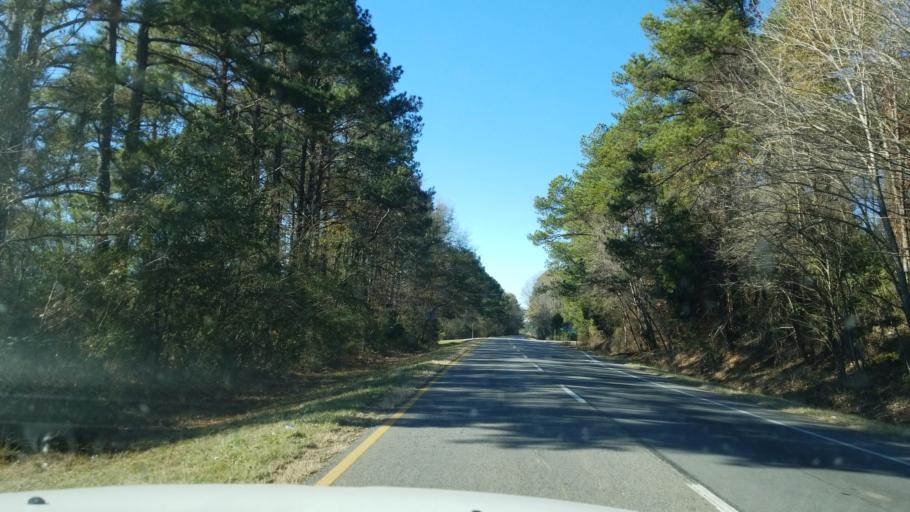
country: US
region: Alabama
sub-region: Tuscaloosa County
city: Northport
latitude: 33.2357
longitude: -87.6475
